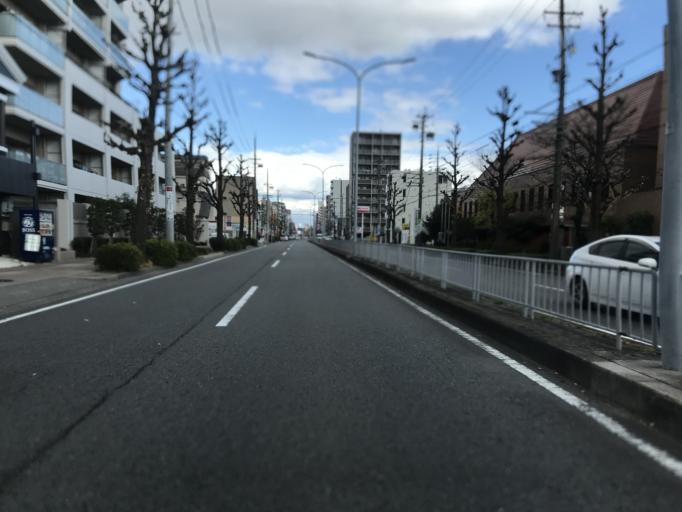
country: JP
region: Aichi
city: Nagoya-shi
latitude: 35.1746
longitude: 136.8642
